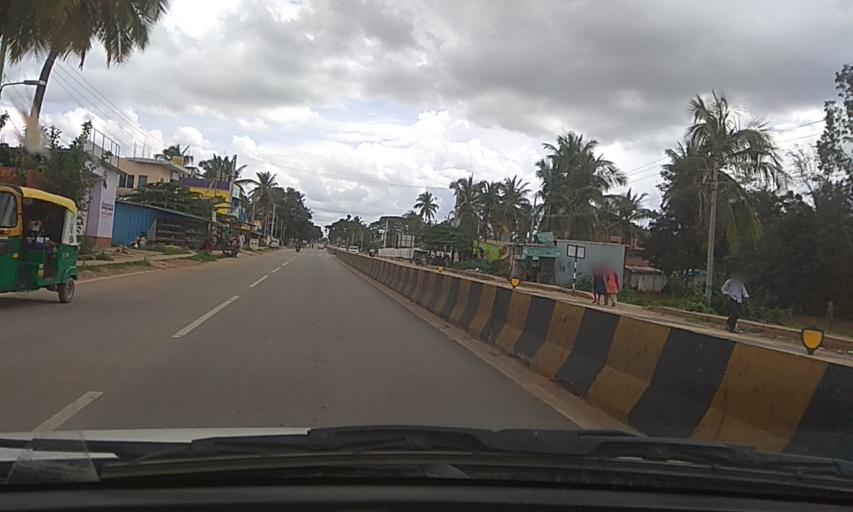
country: IN
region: Karnataka
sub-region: Tumkur
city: Tumkur
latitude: 13.2944
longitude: 77.0913
